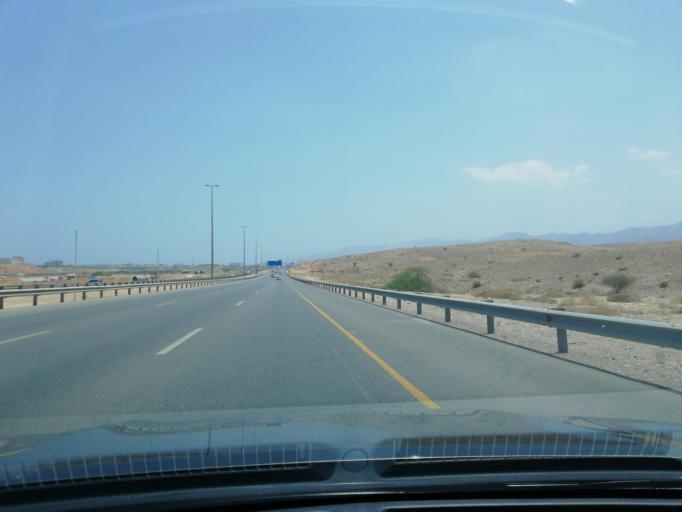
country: OM
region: Muhafazat Masqat
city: Bawshar
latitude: 23.5572
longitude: 58.3149
